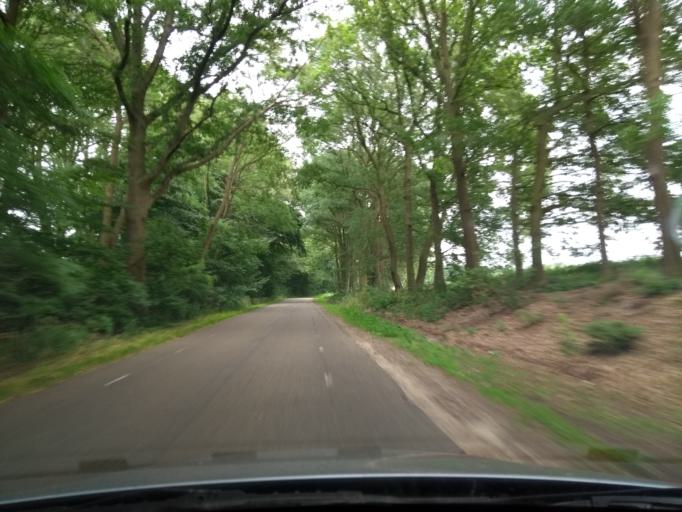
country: NL
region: Overijssel
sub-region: Gemeente Twenterand
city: Den Ham
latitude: 52.4564
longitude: 6.4068
